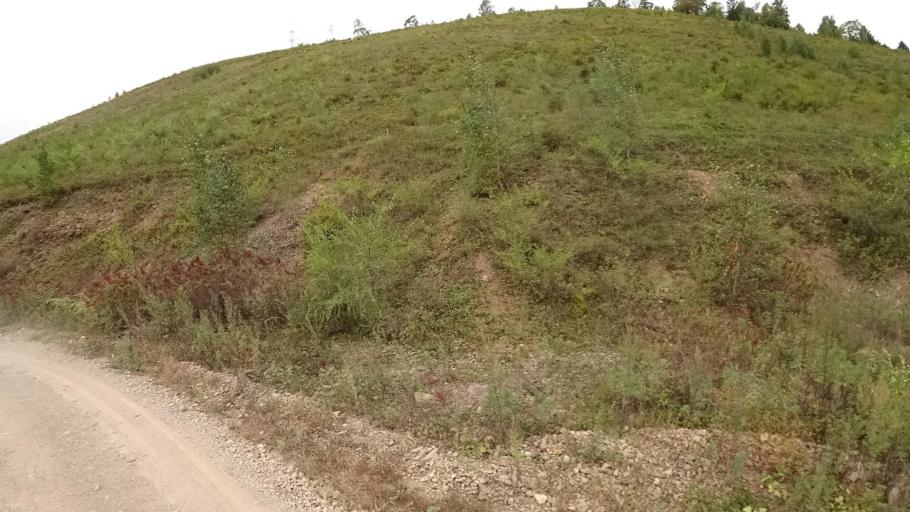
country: RU
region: Jewish Autonomous Oblast
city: Khingansk
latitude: 49.0261
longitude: 131.0736
